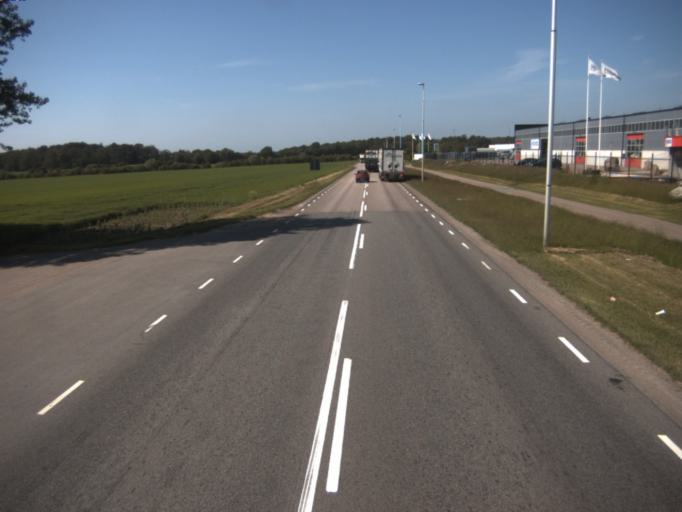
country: SE
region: Skane
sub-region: Helsingborg
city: Barslov
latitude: 56.0448
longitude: 12.7775
